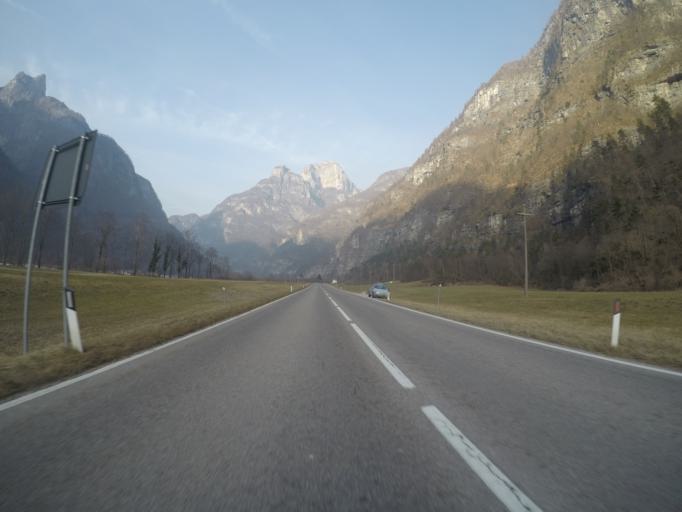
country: IT
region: Veneto
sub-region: Provincia di Belluno
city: Sospirolo
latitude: 46.2005
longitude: 12.1260
